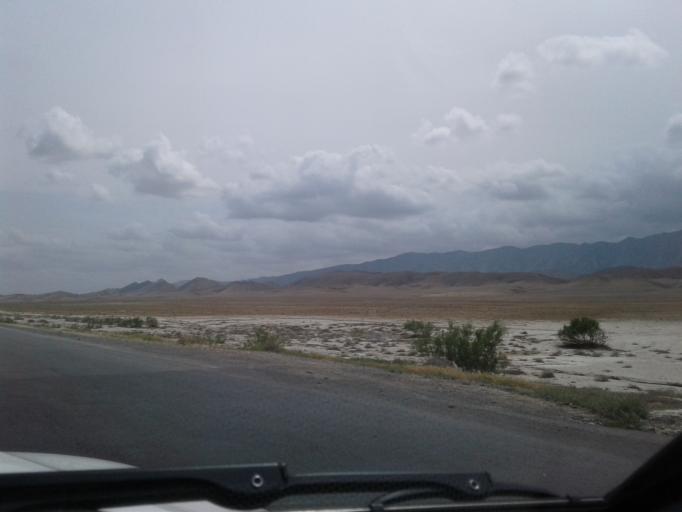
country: IR
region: Razavi Khorasan
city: Dargaz
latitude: 37.7125
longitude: 59.0233
